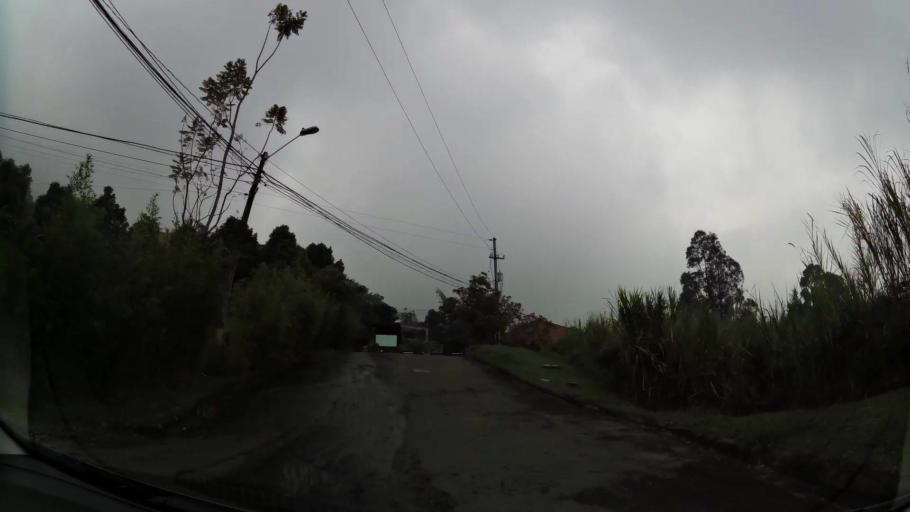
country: CO
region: Antioquia
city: Envigado
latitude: 6.1942
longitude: -75.5527
